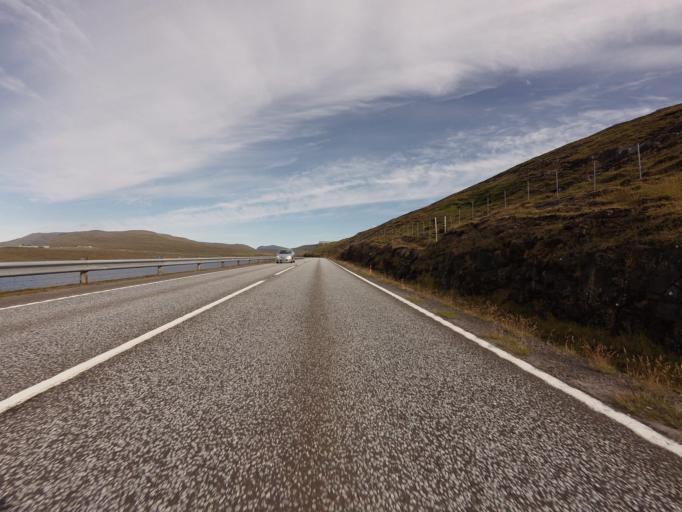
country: FO
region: Vagar
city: Midvagur
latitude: 62.0579
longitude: -7.2412
